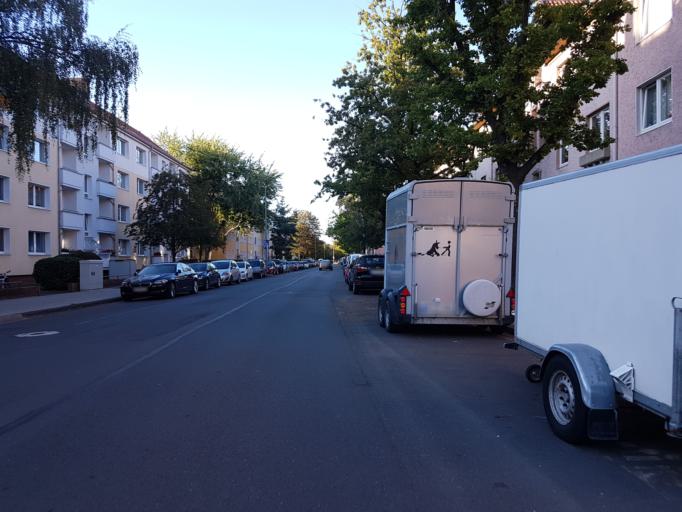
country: DE
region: Lower Saxony
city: Hannover
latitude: 52.4004
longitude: 9.7406
